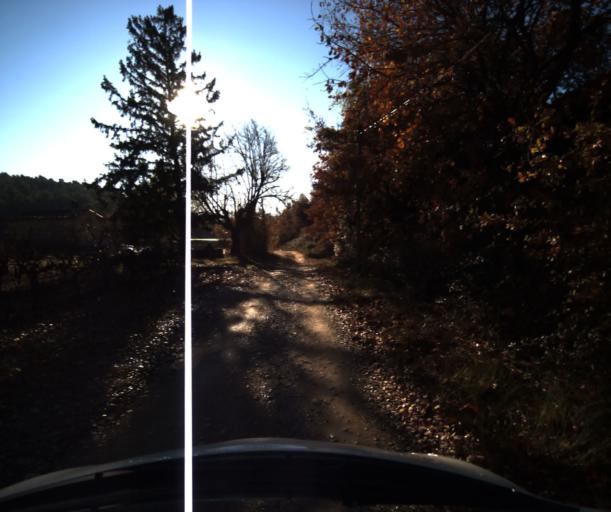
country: FR
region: Provence-Alpes-Cote d'Azur
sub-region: Departement du Vaucluse
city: Pertuis
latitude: 43.7187
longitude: 5.4943
